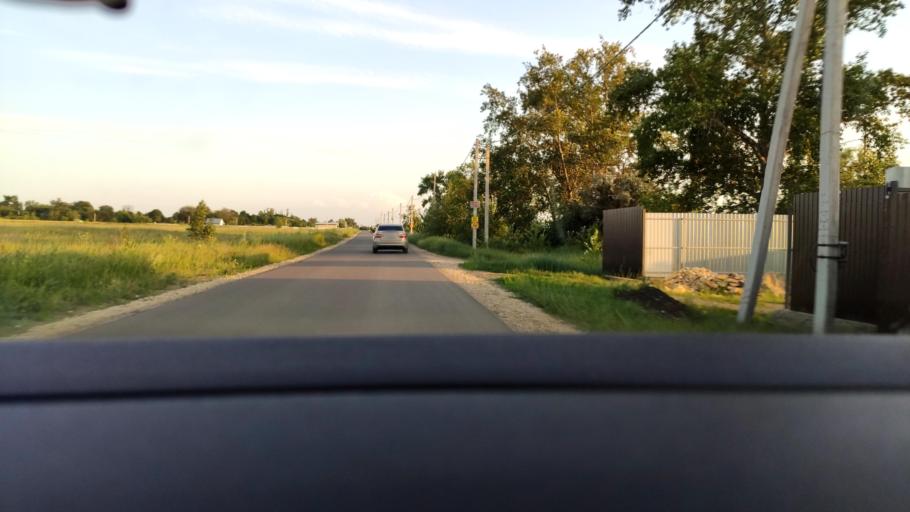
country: RU
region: Voronezj
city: Ramon'
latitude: 51.8968
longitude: 39.1760
